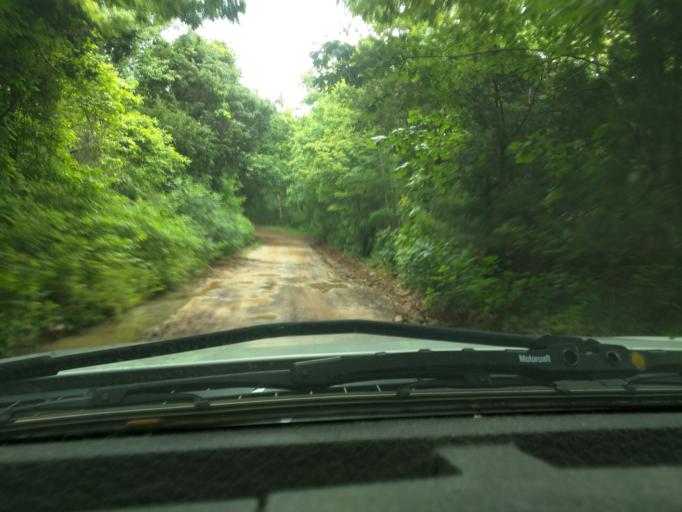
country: US
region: Arkansas
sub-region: Madison County
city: Huntsville
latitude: 35.8883
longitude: -93.5602
